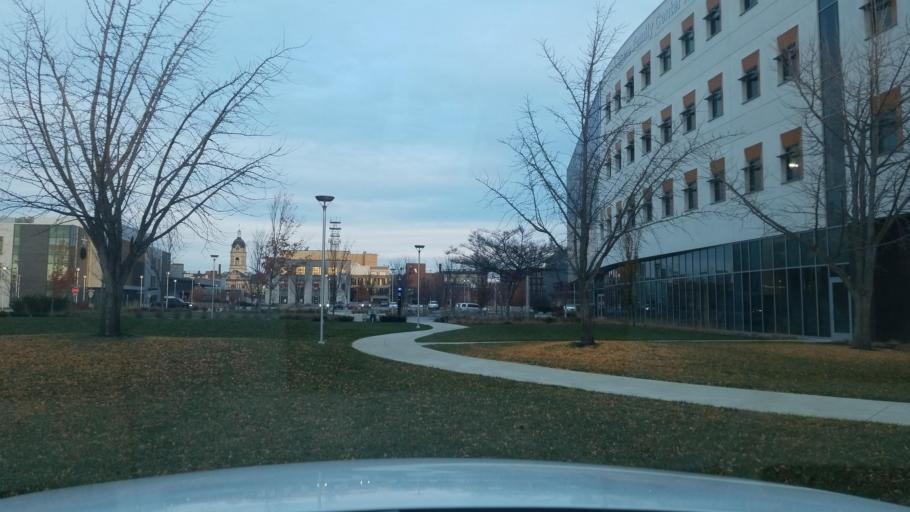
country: US
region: Indiana
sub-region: Vanderburgh County
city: Evansville
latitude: 37.9698
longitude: -87.5676
